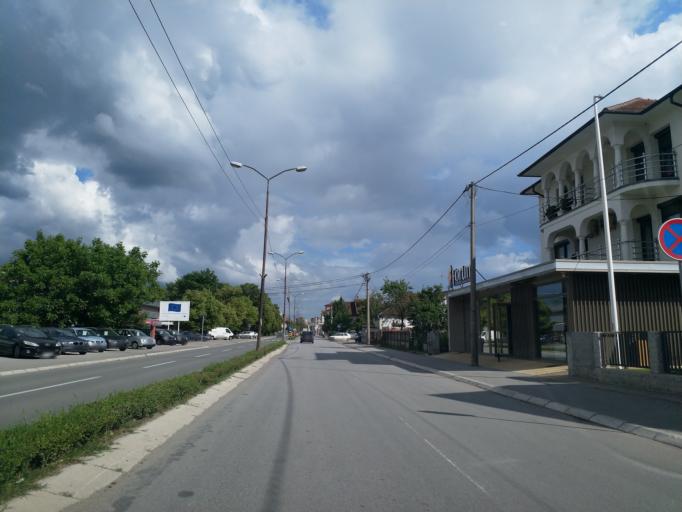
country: RS
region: Central Serbia
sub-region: Pomoravski Okrug
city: Paracin
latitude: 43.8695
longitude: 21.4030
